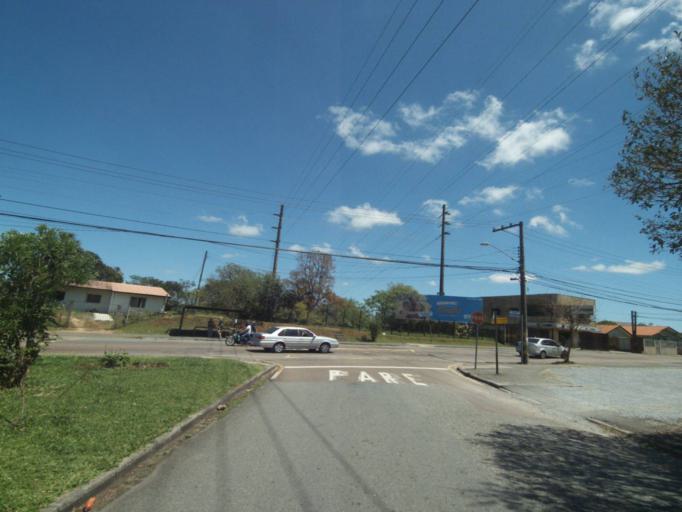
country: BR
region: Parana
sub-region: Curitiba
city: Curitiba
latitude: -25.3746
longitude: -49.2629
